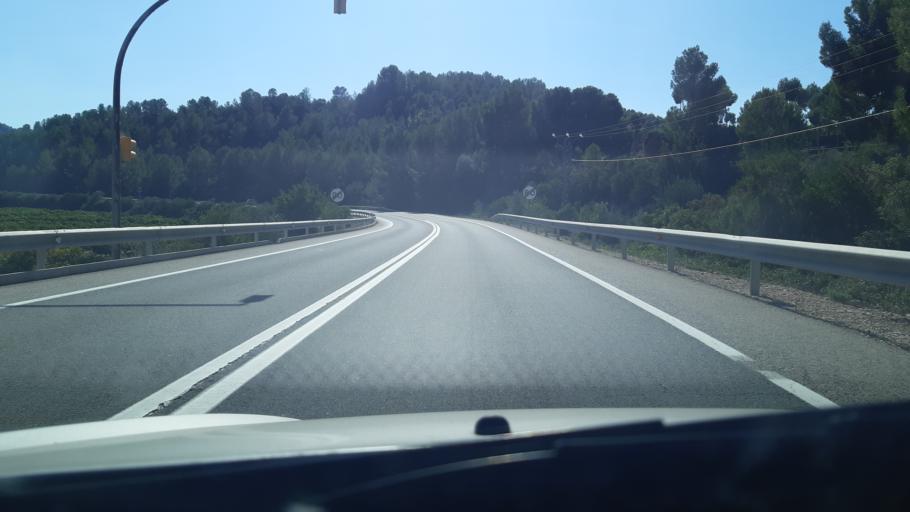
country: ES
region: Catalonia
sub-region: Provincia de Tarragona
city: Benifallet
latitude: 40.9479
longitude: 0.4835
